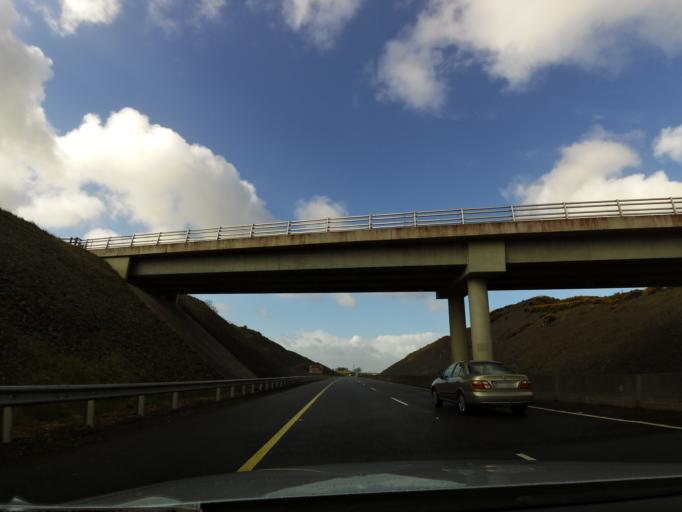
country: IE
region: Munster
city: Ballina
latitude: 52.7711
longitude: -8.3845
